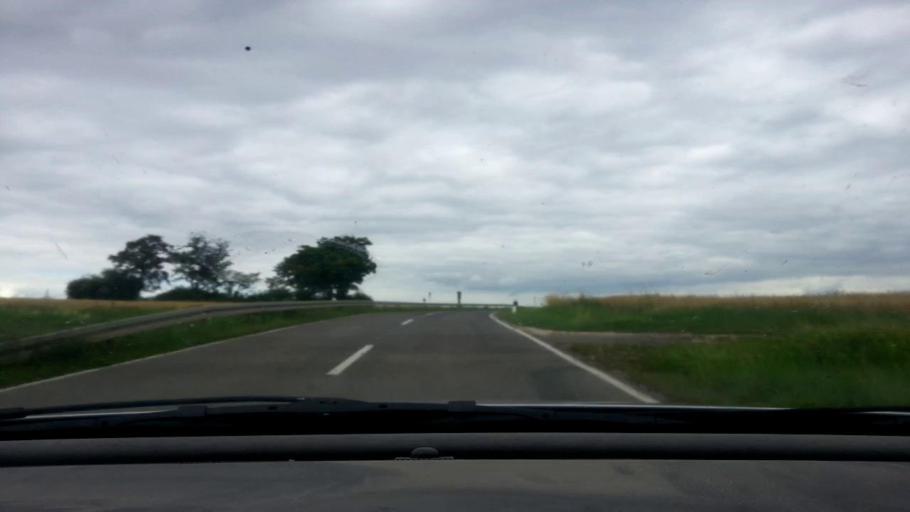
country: DE
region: Bavaria
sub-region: Upper Franconia
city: Gundelsheim
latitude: 49.9627
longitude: 10.9352
